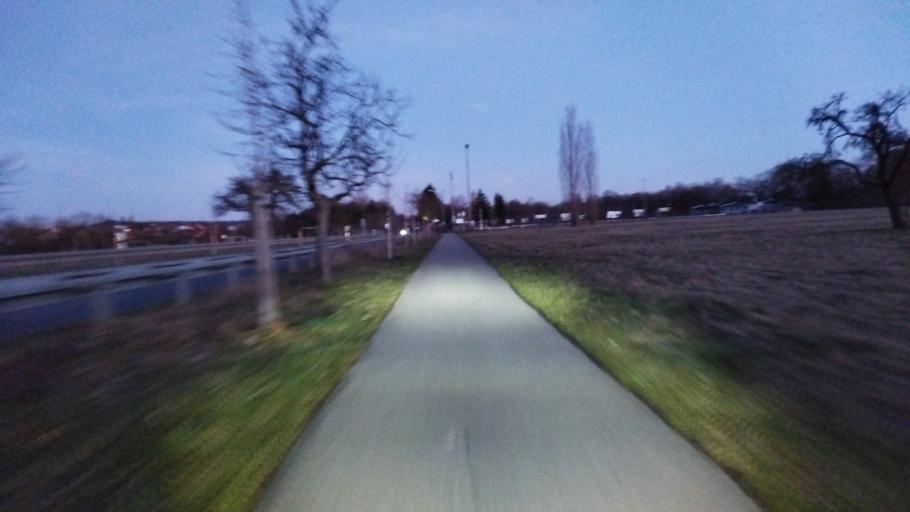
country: DE
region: Bavaria
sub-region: Regierungsbezirk Unterfranken
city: Volkach
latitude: 49.8715
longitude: 10.2156
